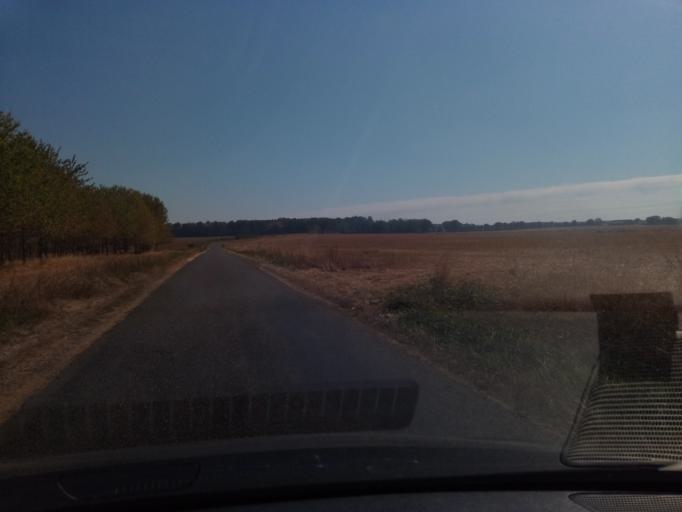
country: FR
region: Poitou-Charentes
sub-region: Departement de la Vienne
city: Lussac-les-Chateaux
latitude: 46.3821
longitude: 0.7840
